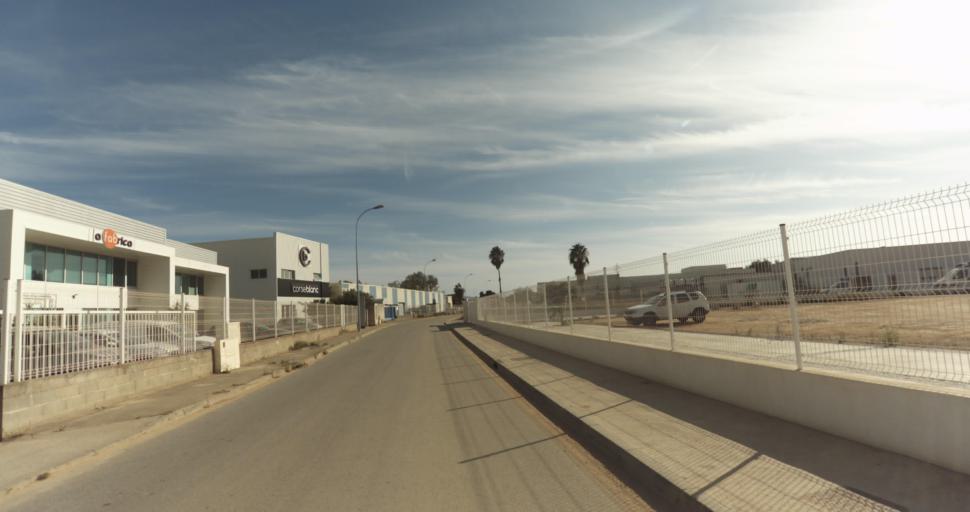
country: FR
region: Corsica
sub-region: Departement de la Corse-du-Sud
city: Afa
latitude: 41.9311
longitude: 8.7899
